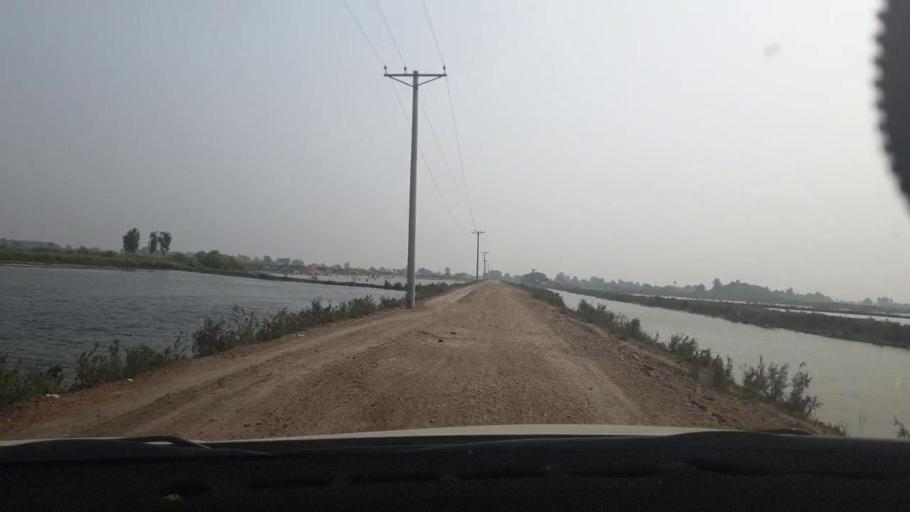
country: PK
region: Sindh
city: Tando Muhammad Khan
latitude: 25.0781
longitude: 68.4948
